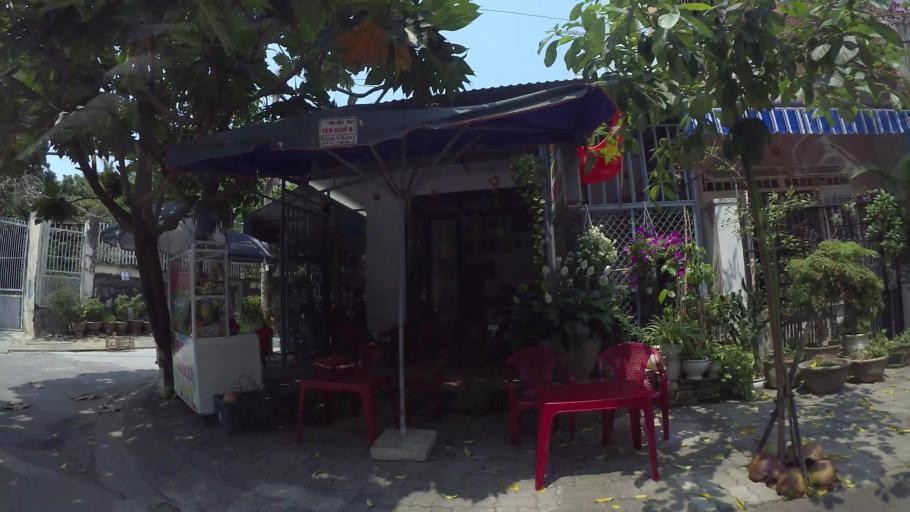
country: VN
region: Da Nang
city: Cam Le
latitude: 16.0182
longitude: 108.2091
